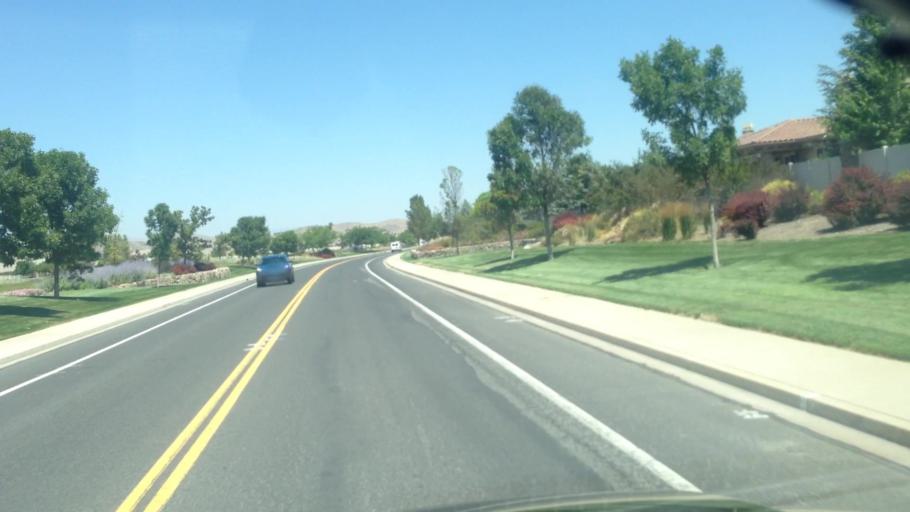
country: US
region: Nevada
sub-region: Washoe County
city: Sparks
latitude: 39.4279
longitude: -119.7152
